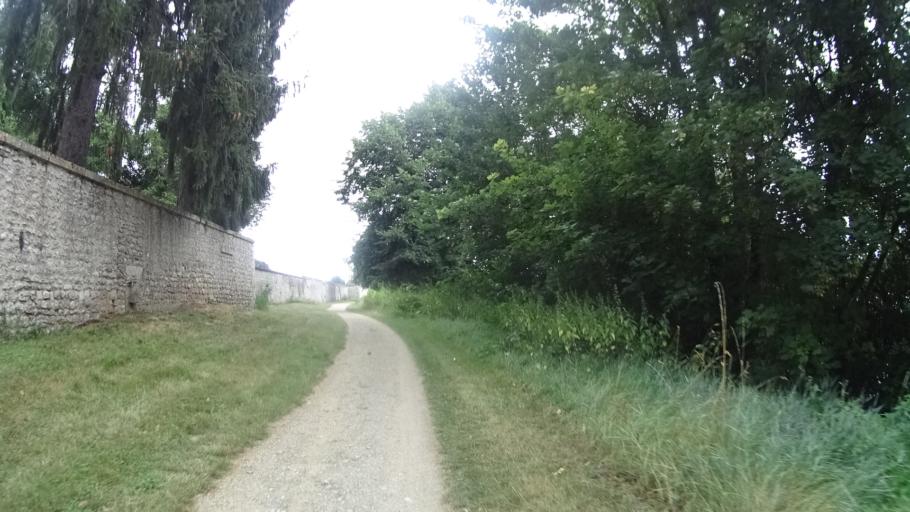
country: FR
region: Centre
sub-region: Departement du Loir-et-Cher
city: Montlivault
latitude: 47.6438
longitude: 1.4189
